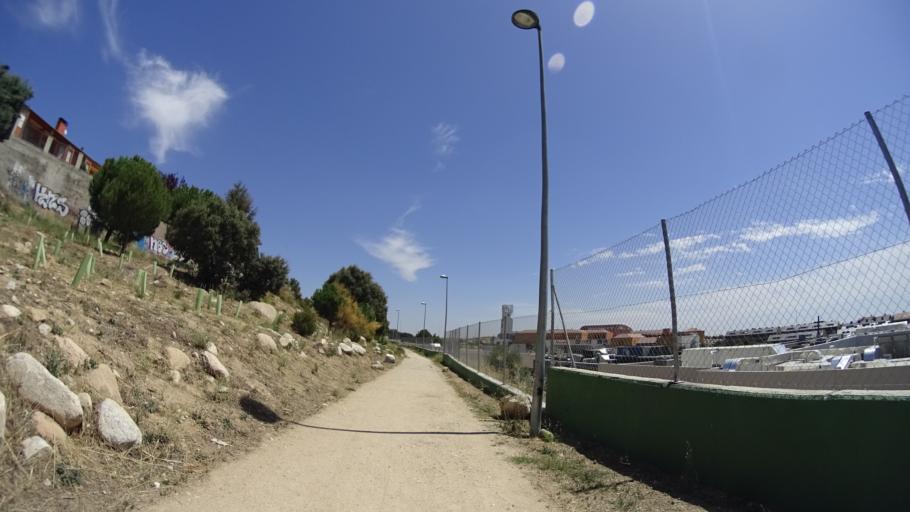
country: ES
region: Madrid
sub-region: Provincia de Madrid
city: Torrelodones
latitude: 40.5681
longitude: -3.9247
